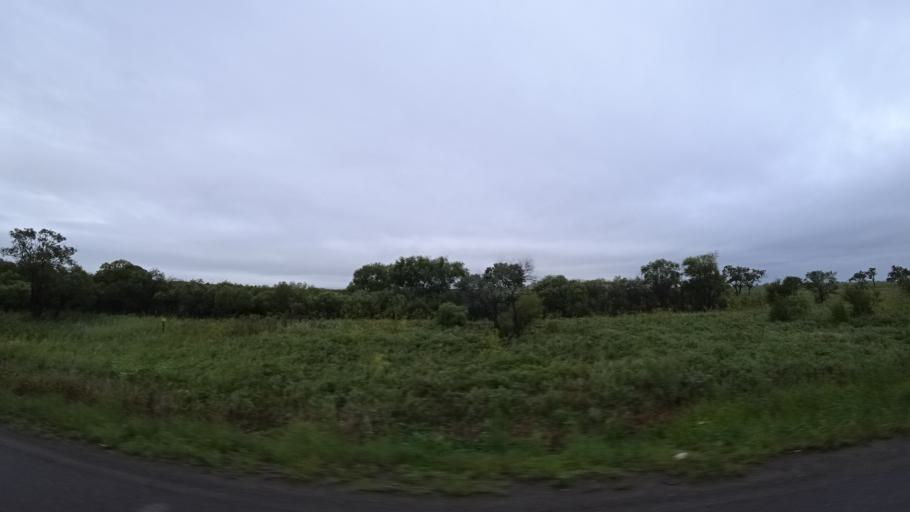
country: RU
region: Primorskiy
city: Chernigovka
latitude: 44.2906
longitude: 132.5080
